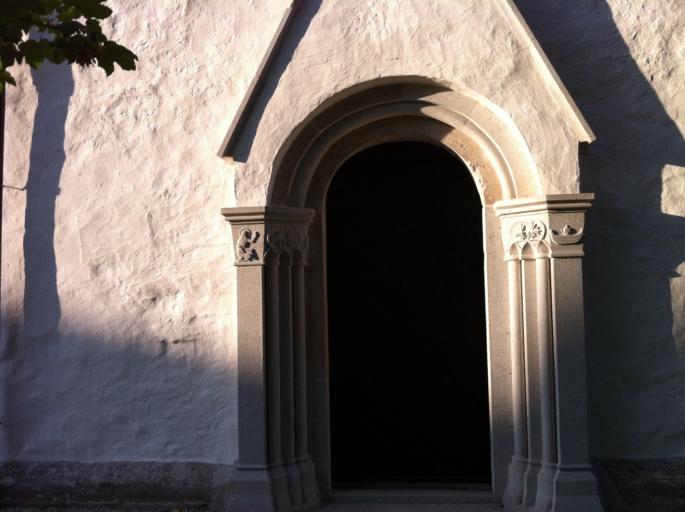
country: SE
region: Gotland
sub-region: Gotland
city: Slite
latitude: 57.4217
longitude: 18.8586
